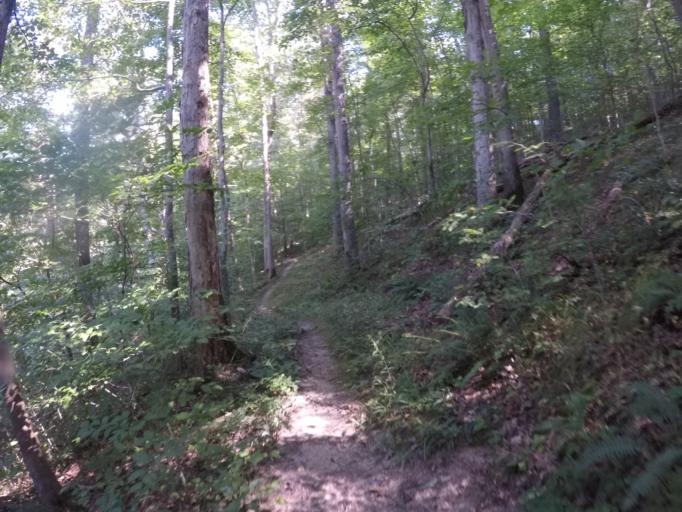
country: US
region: Ohio
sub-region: Lawrence County
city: Ironton
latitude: 38.6245
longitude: -82.6170
